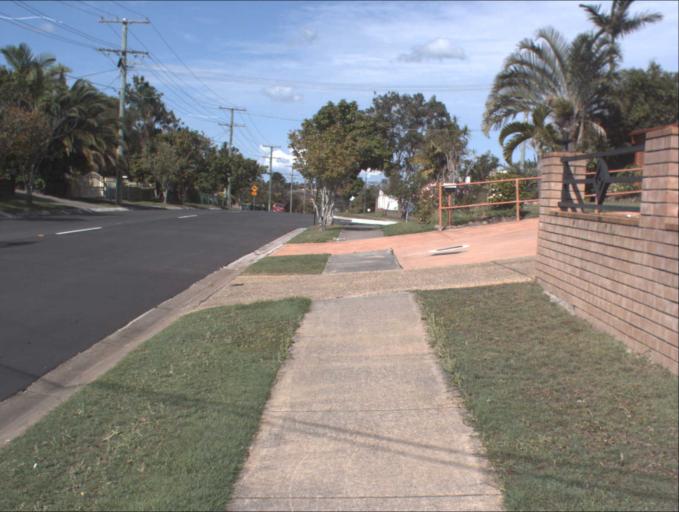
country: AU
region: Queensland
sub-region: Brisbane
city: Sunnybank Hills
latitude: -27.6633
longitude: 153.0541
